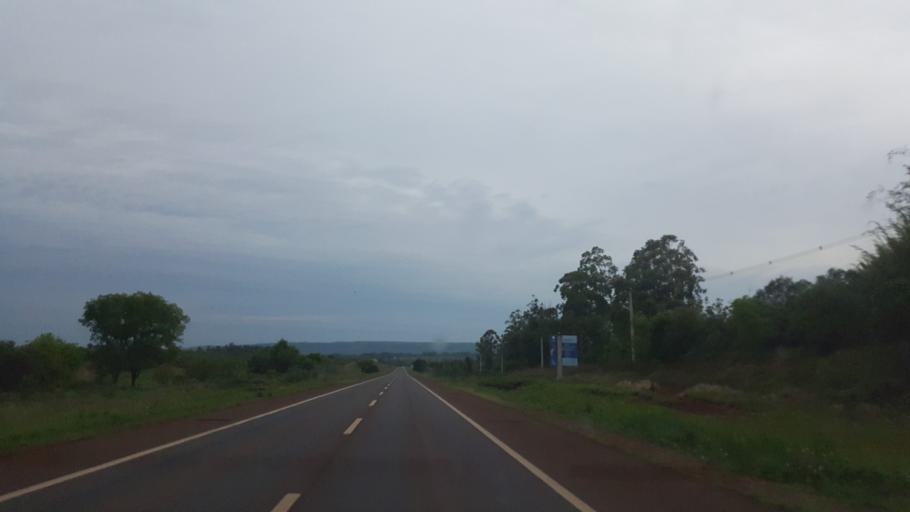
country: AR
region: Misiones
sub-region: Departamento de Apostoles
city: San Jose
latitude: -27.7756
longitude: -55.8089
